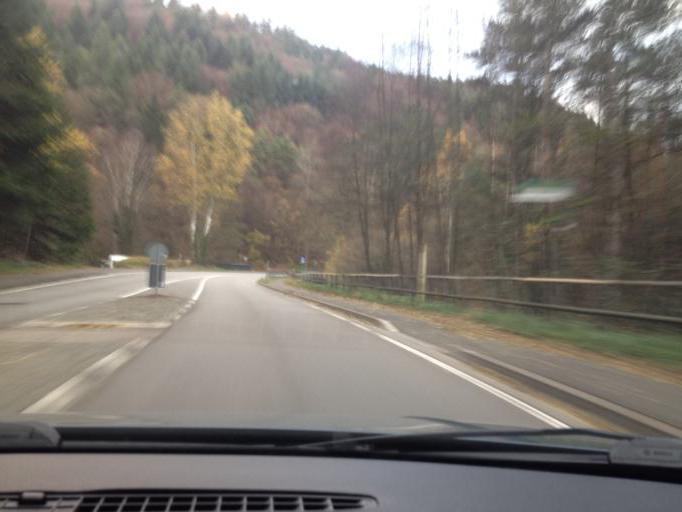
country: DE
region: Rheinland-Pfalz
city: Frankenstein
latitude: 49.4302
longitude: 7.9793
